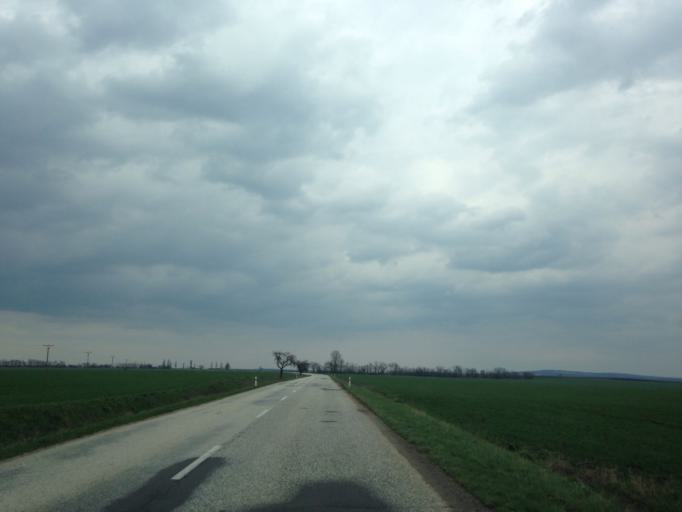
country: SK
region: Nitriansky
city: Svodin
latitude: 47.9834
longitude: 18.3655
